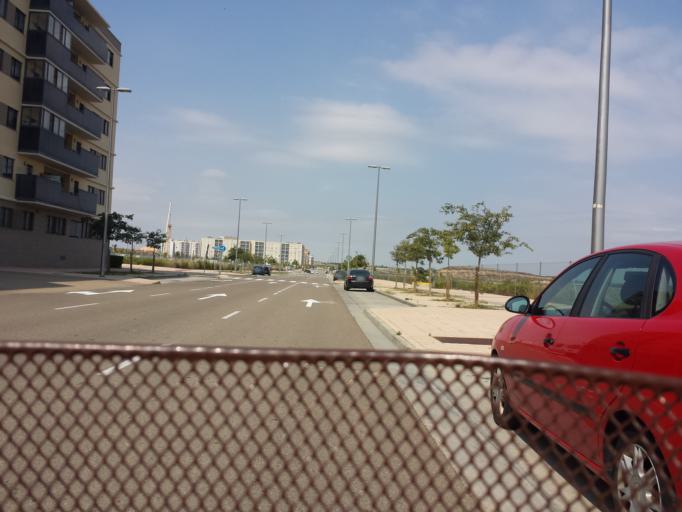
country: ES
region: Aragon
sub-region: Provincia de Zaragoza
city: Montecanal
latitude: 41.6245
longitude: -0.9526
